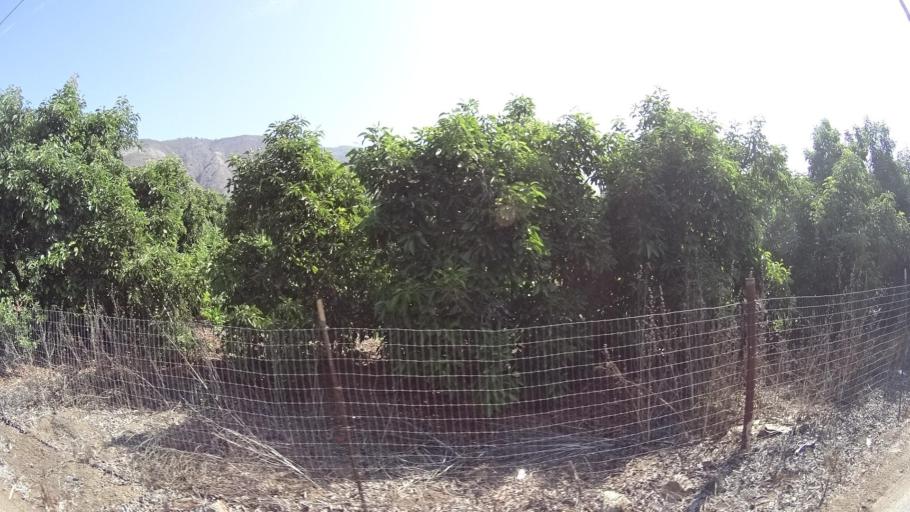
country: US
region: California
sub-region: San Diego County
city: Valley Center
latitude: 33.3351
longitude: -116.9893
